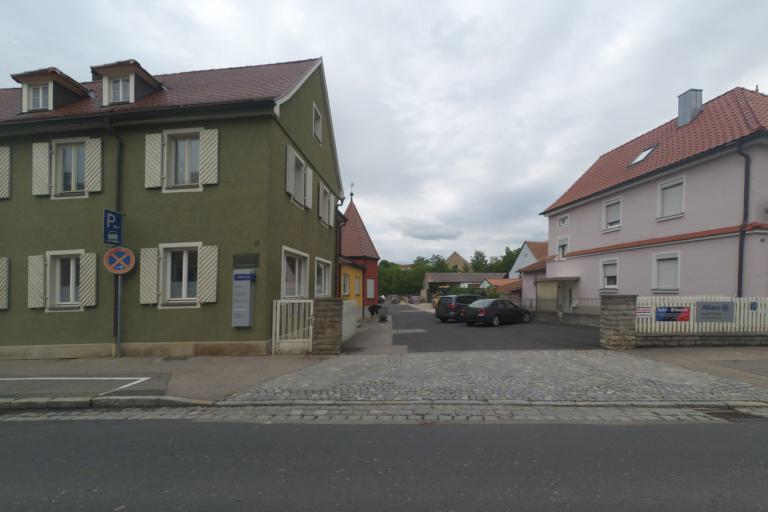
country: DE
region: Bavaria
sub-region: Regierungsbezirk Mittelfranken
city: Uffenheim
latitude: 49.5478
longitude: 10.2378
